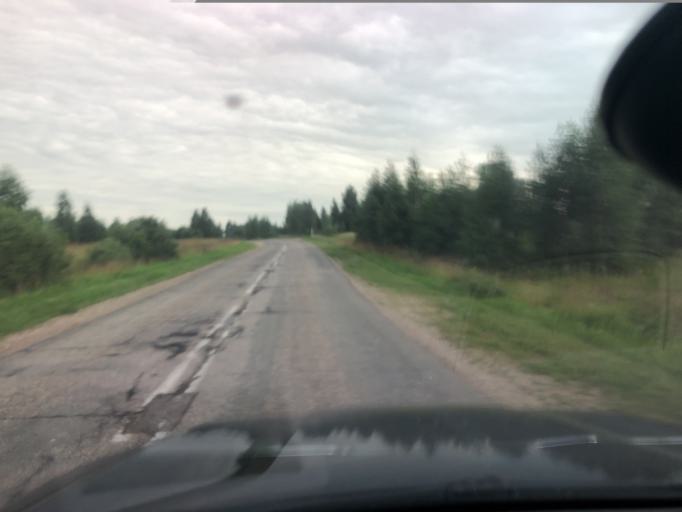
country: RU
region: Jaroslavl
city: Petrovsk
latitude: 57.0009
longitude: 39.0434
